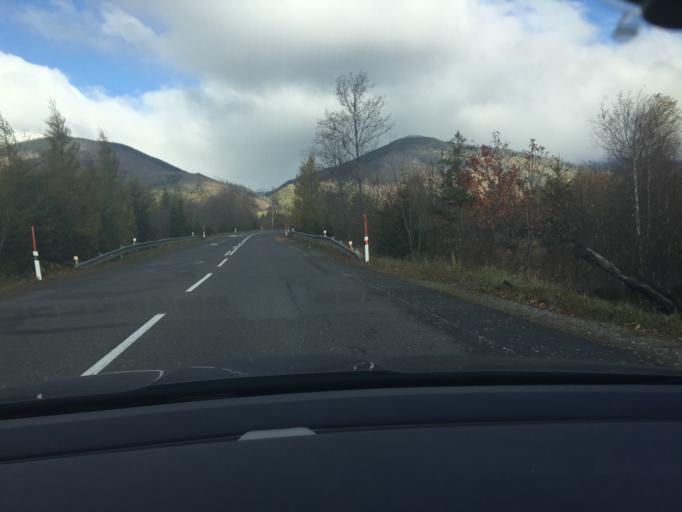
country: SK
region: Presovsky
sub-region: Okres Poprad
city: Nova Lesna
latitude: 49.1809
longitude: 20.2911
